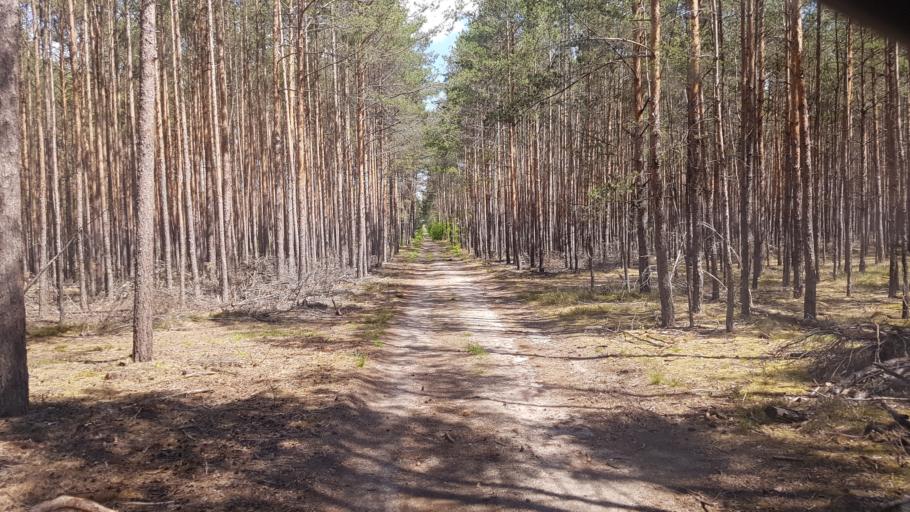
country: DE
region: Brandenburg
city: Sonnewalde
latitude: 51.6534
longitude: 13.6641
